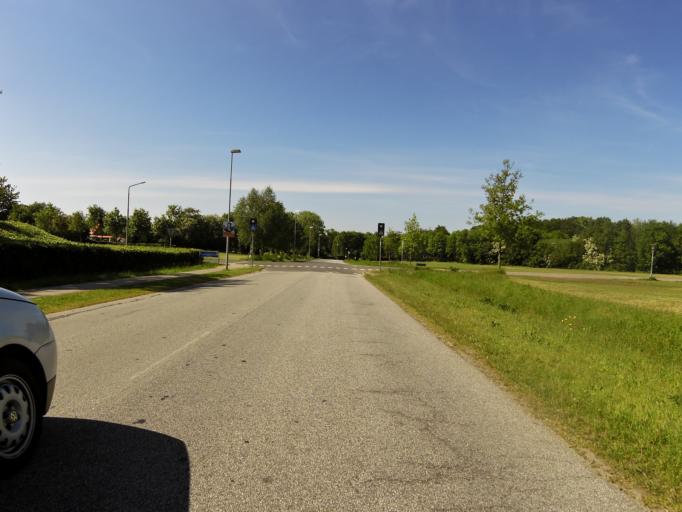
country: DK
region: South Denmark
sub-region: Haderslev Kommune
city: Gram
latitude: 55.2897
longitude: 9.0570
